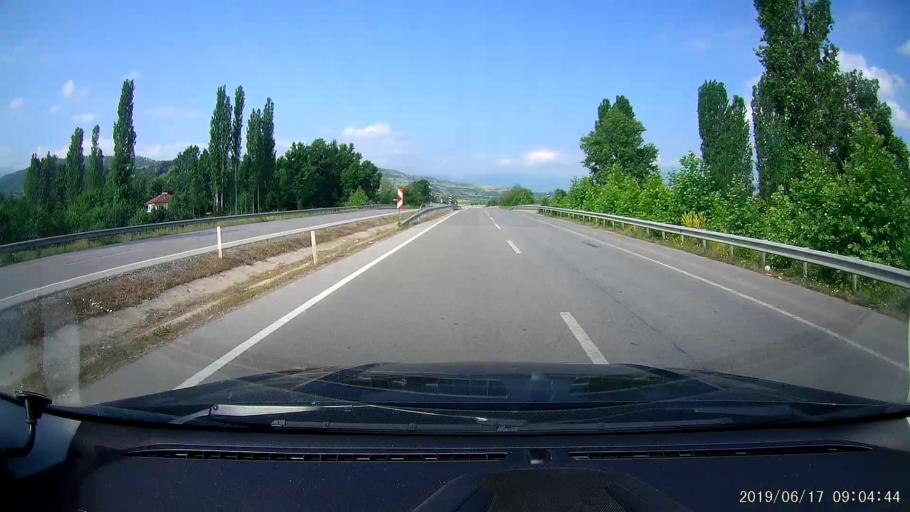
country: TR
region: Amasya
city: Tasova
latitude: 40.7428
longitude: 36.2816
